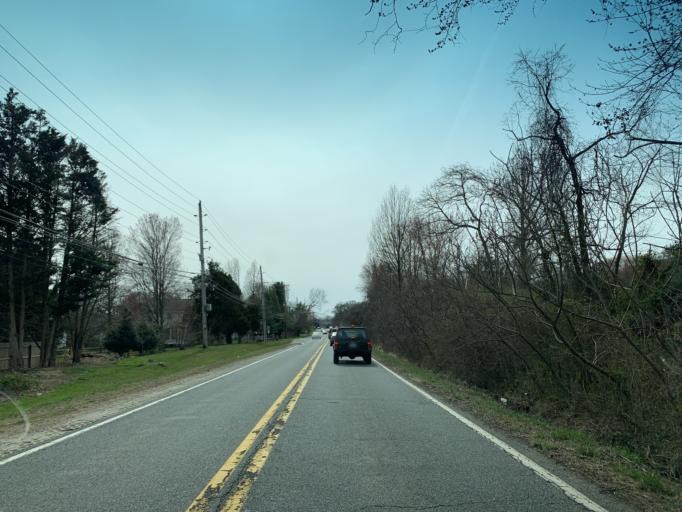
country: US
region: Delaware
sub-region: New Castle County
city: Brookside
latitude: 39.6385
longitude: -75.7395
